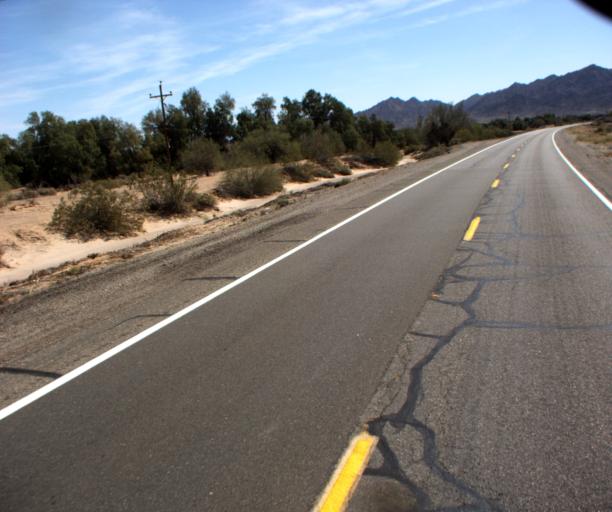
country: US
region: Arizona
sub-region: Yuma County
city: Fortuna Foothills
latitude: 32.7879
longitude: -114.3813
